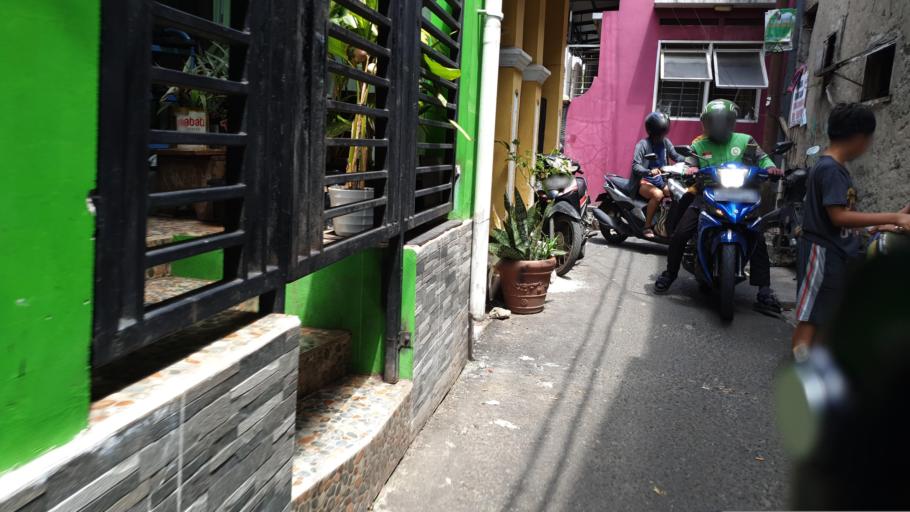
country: ID
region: Jakarta Raya
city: Jakarta
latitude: -6.2492
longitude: 106.7889
